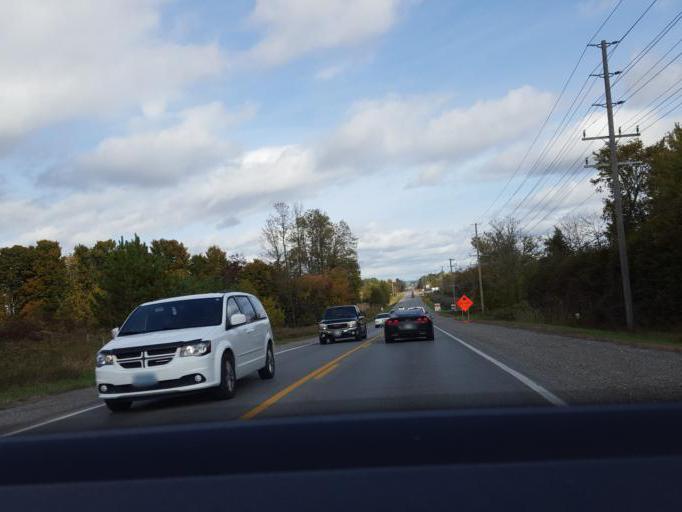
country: CA
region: Ontario
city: Oshawa
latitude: 43.9550
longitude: -78.7826
